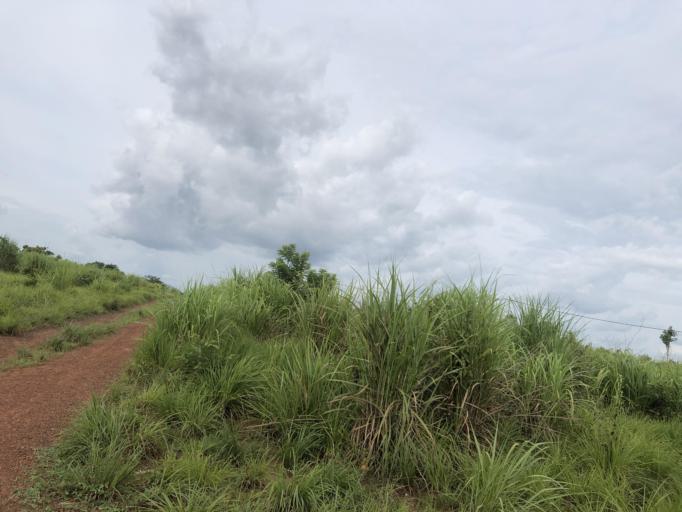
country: SL
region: Northern Province
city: Magburaka
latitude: 8.7327
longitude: -11.9150
